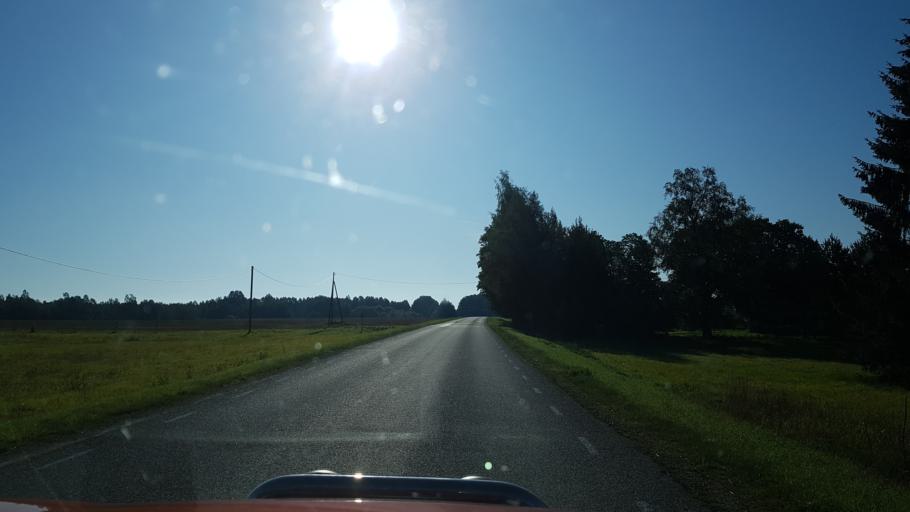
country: EE
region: Jogevamaa
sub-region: Tabivere vald
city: Tabivere
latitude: 58.6823
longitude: 26.6146
